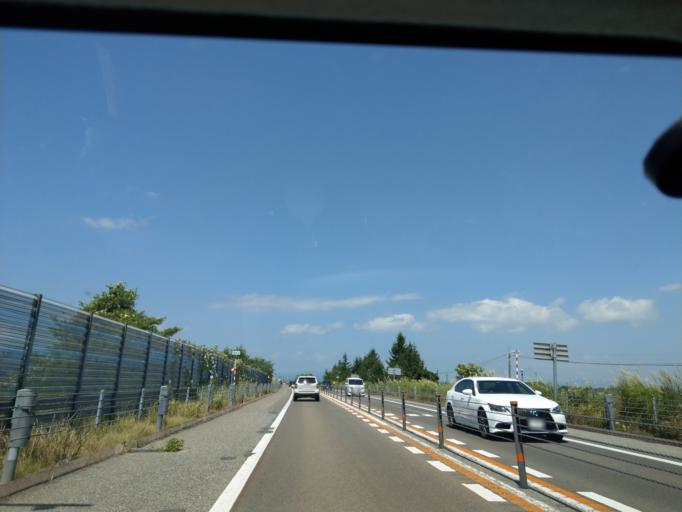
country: JP
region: Akita
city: Omagari
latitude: 39.3898
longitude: 140.4788
